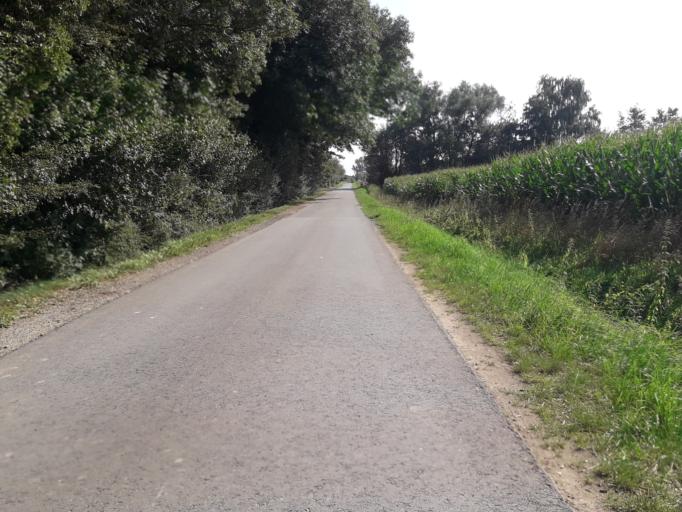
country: DE
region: North Rhine-Westphalia
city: Bad Lippspringe
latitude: 51.7607
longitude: 8.8034
